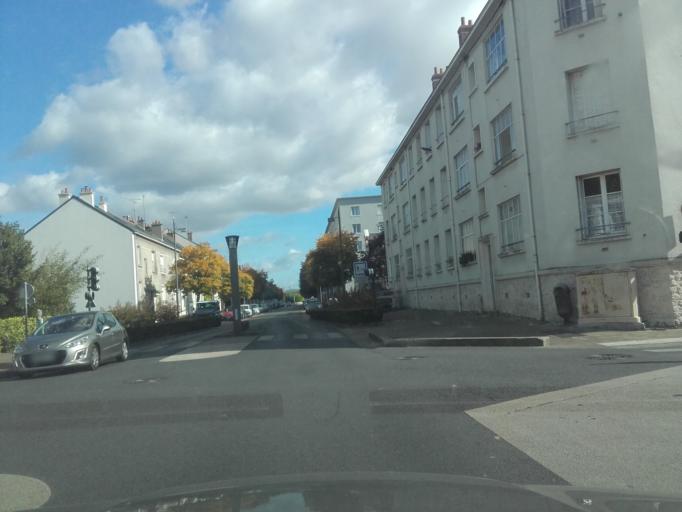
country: FR
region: Centre
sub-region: Departement d'Indre-et-Loire
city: Saint-Pierre-des-Corps
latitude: 47.3874
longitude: 0.7230
